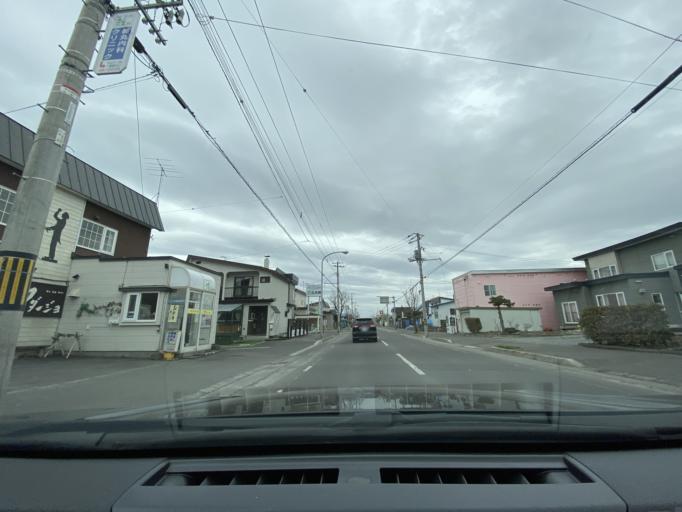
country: JP
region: Hokkaido
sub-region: Asahikawa-shi
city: Asahikawa
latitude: 43.7932
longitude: 142.4172
